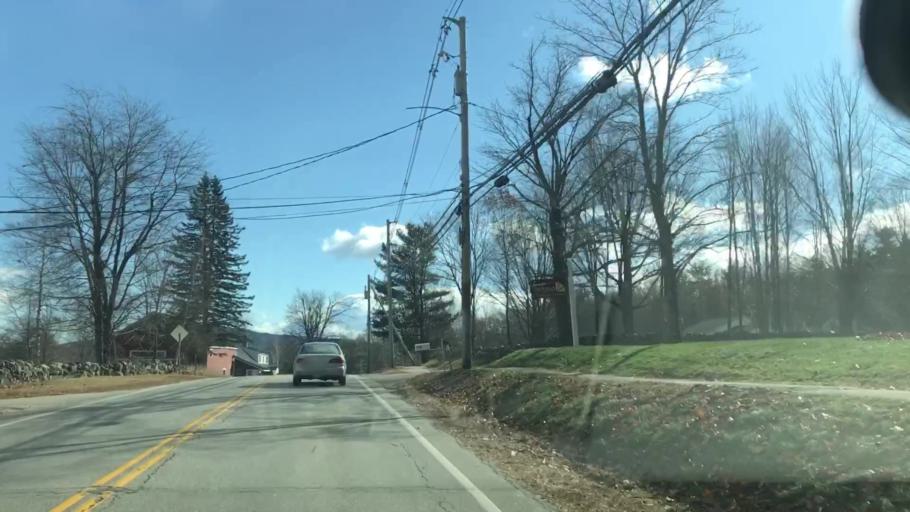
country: US
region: New Hampshire
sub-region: Carroll County
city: Wolfeboro
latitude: 43.5698
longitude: -71.1819
